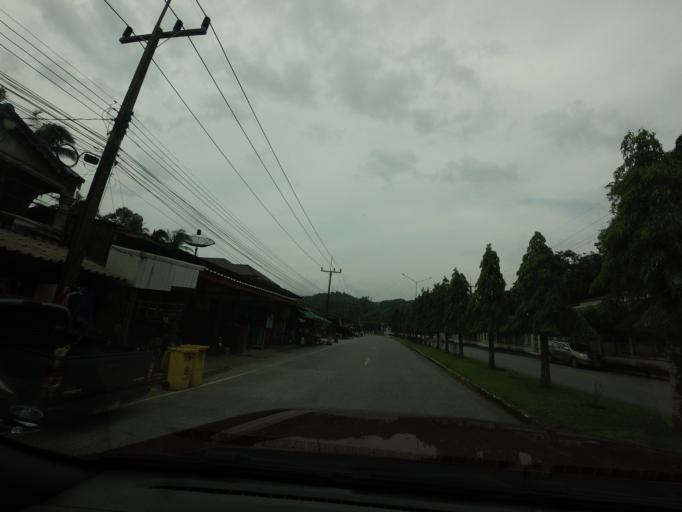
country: TH
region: Yala
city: Than To
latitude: 6.1611
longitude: 101.2723
